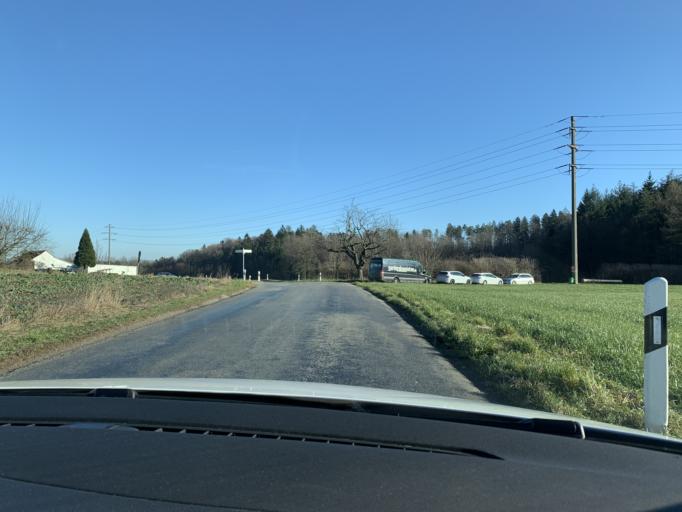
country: CH
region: Zurich
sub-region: Bezirk Dielsdorf
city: Sonnhalde
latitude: 47.4642
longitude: 8.4499
